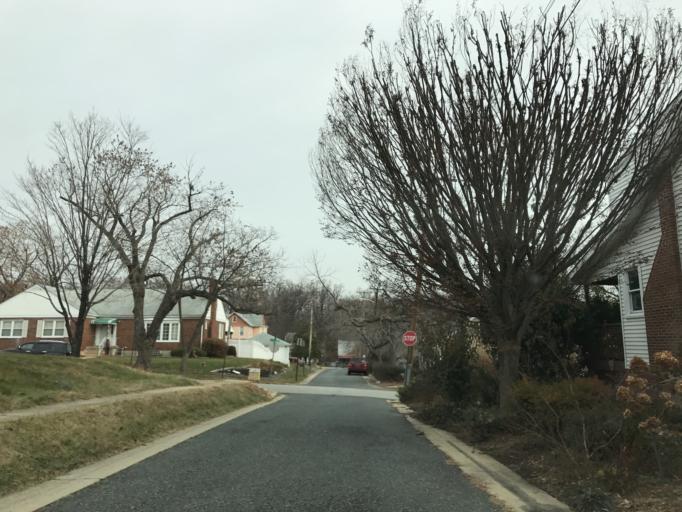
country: US
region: Maryland
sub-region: Baltimore County
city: Overlea
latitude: 39.3588
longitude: -76.5318
